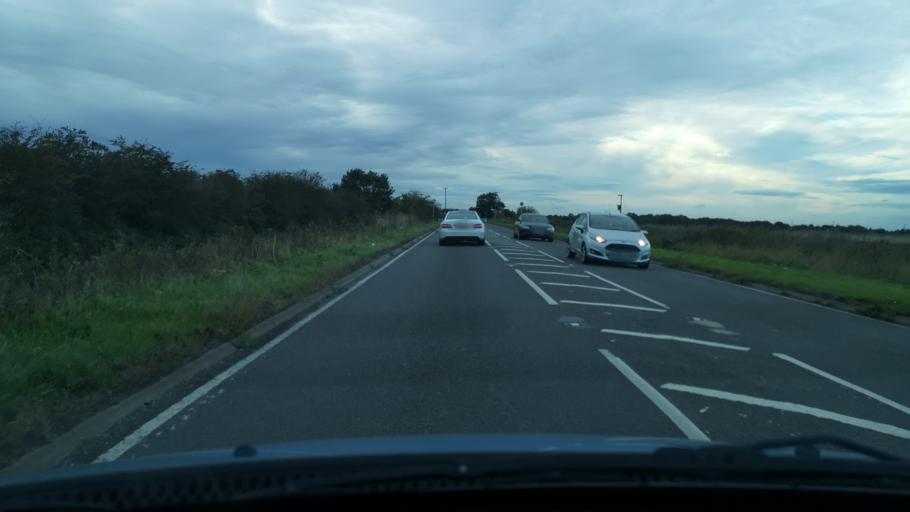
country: GB
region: England
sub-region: North Lincolnshire
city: Belton
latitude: 53.5806
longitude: -0.7885
